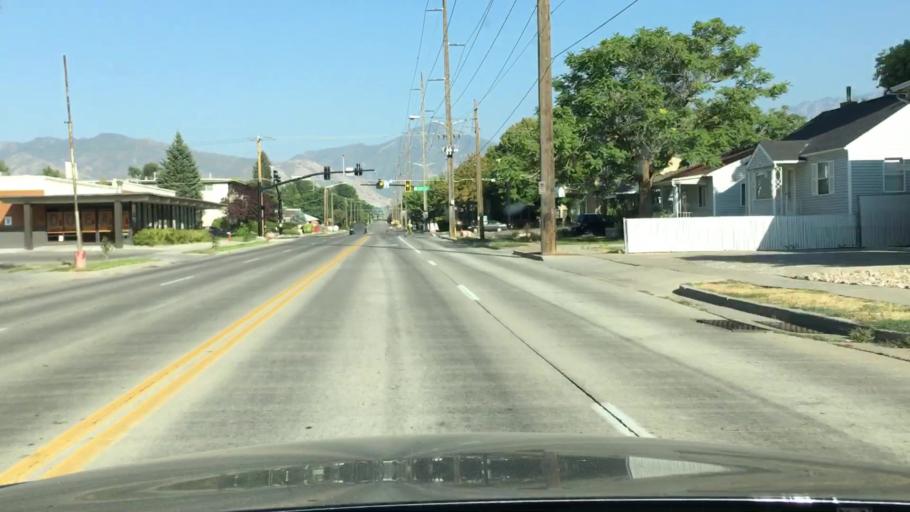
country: US
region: Utah
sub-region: Salt Lake County
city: South Salt Lake
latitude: 40.7126
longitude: -111.8838
